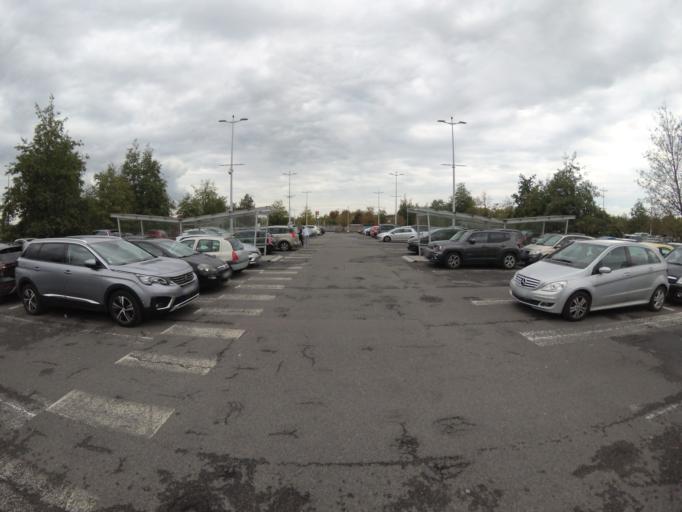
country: FR
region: Ile-de-France
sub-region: Departement de Seine-et-Marne
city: Serris
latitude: 48.8541
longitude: 2.7771
